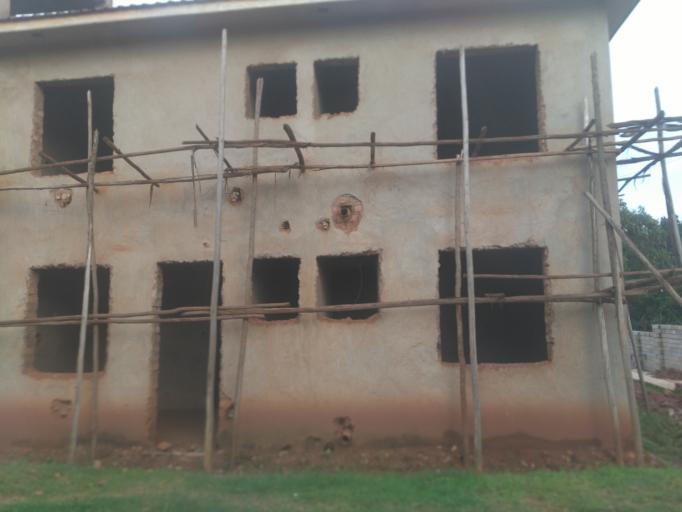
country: UG
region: Central Region
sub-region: Wakiso District
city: Kireka
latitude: 0.3767
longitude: 32.6161
